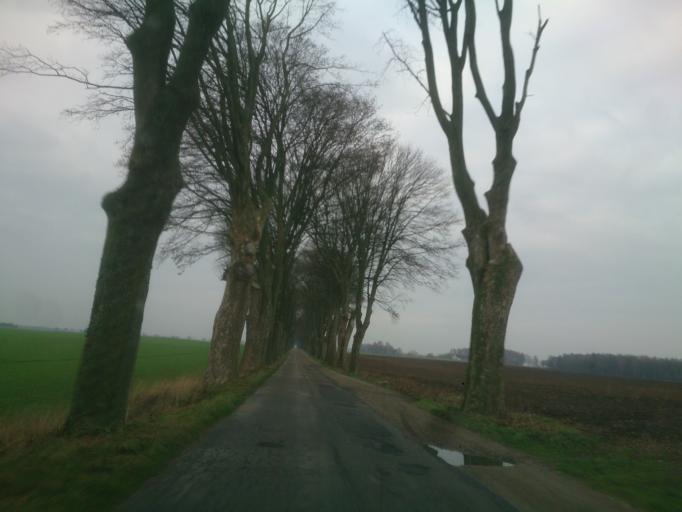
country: PL
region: West Pomeranian Voivodeship
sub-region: Powiat slawienski
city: Slawno
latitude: 54.3144
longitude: 16.6072
